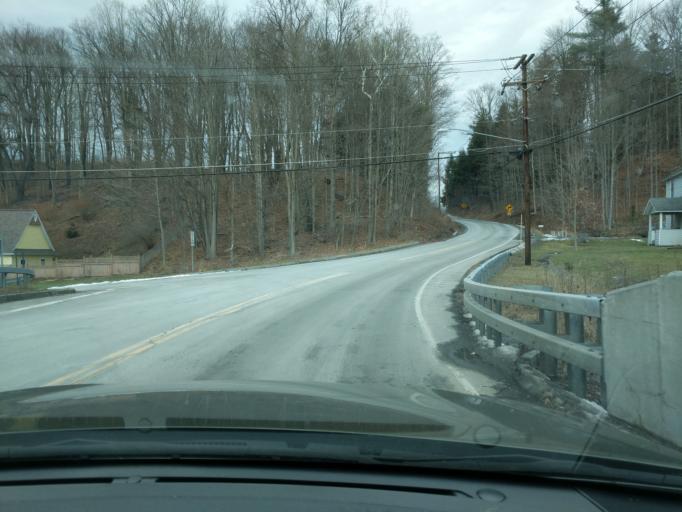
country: US
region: New York
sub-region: Tompkins County
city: East Ithaca
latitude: 42.3818
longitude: -76.3881
